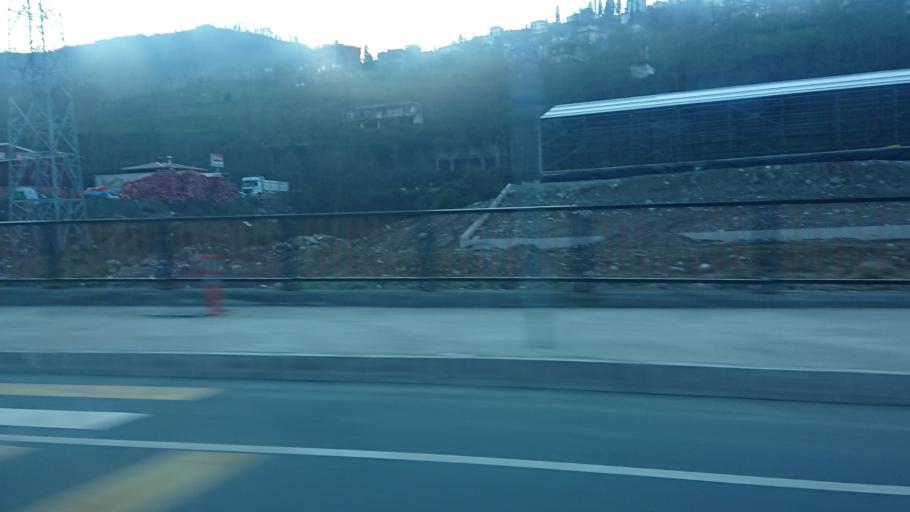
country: TR
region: Rize
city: Gundogdu
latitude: 41.0281
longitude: 40.5830
